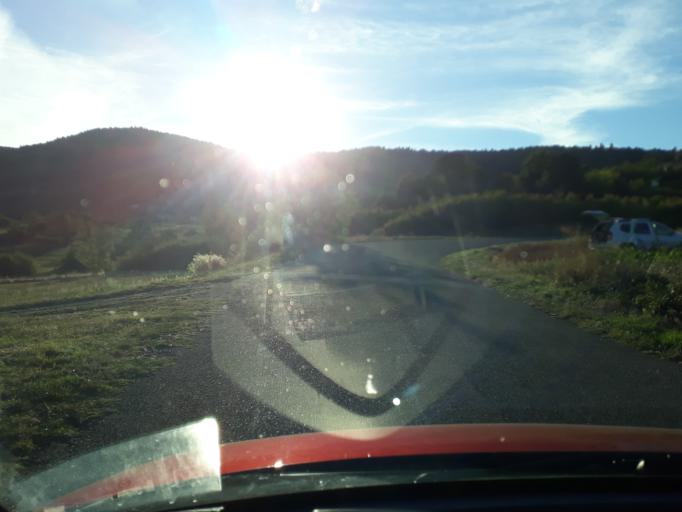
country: FR
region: Rhone-Alpes
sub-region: Departement de l'Ardeche
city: Felines
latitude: 45.3270
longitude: 4.7073
